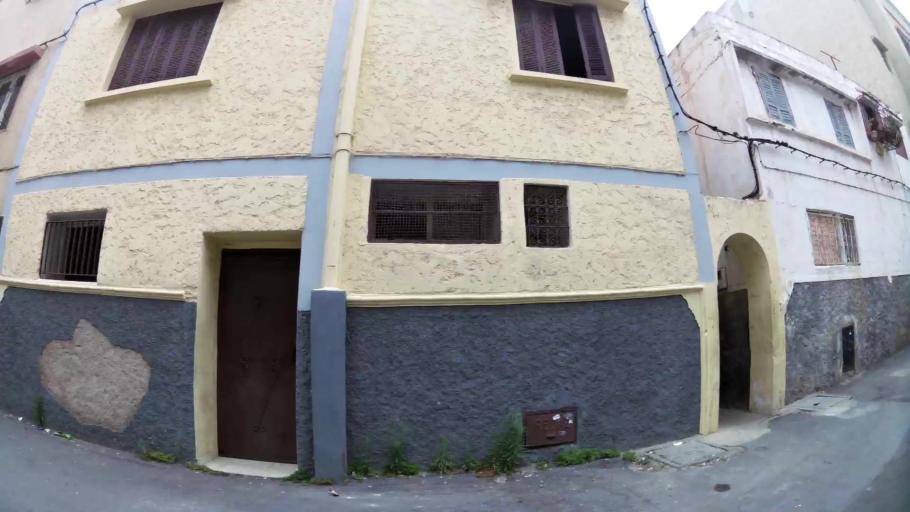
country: MA
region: Rabat-Sale-Zemmour-Zaer
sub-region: Rabat
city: Rabat
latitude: 34.0001
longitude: -6.8706
